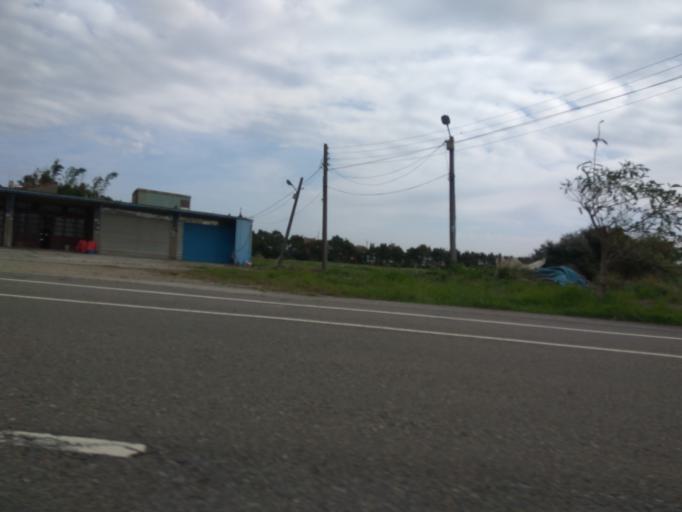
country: TW
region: Taiwan
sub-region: Hsinchu
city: Zhubei
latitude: 24.9790
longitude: 121.0270
